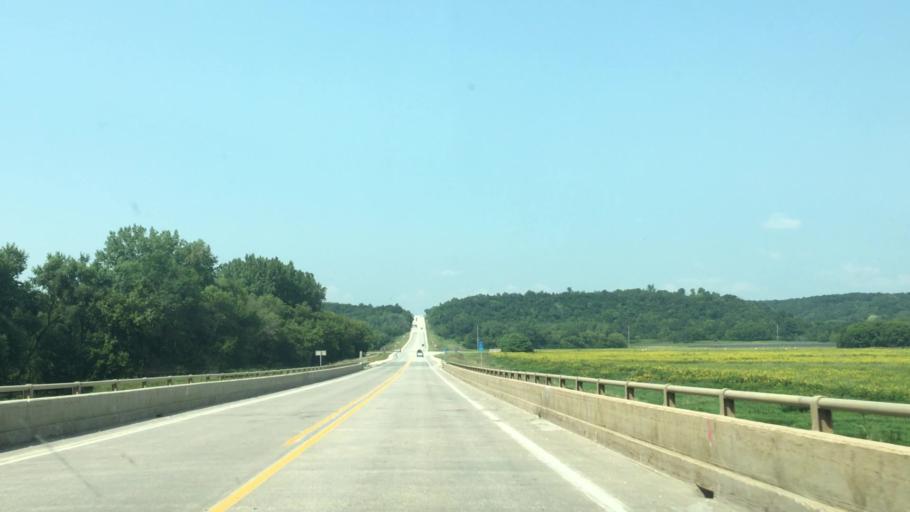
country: US
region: Iowa
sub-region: Winneshiek County
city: Decorah
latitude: 43.3156
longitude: -91.8143
